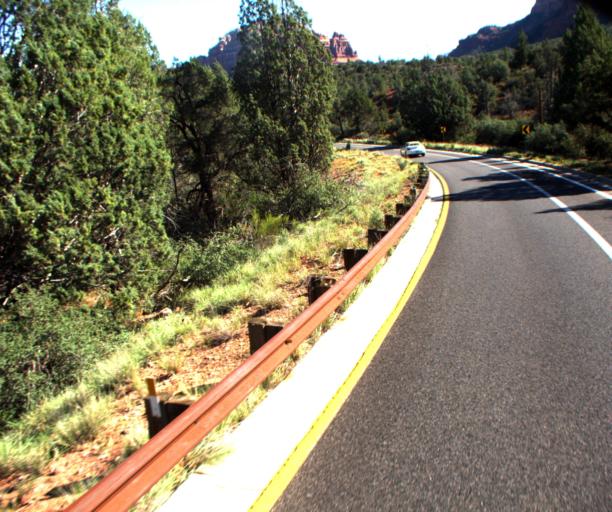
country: US
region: Arizona
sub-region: Yavapai County
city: Village of Oak Creek (Big Park)
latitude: 34.8103
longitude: -111.7651
